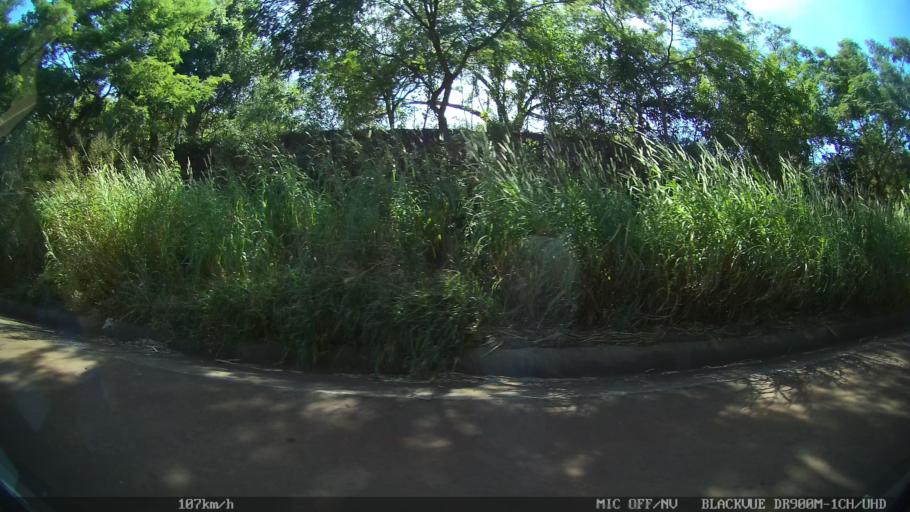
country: BR
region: Sao Paulo
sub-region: Sao Joaquim Da Barra
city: Sao Joaquim da Barra
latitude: -20.5533
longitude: -47.6662
